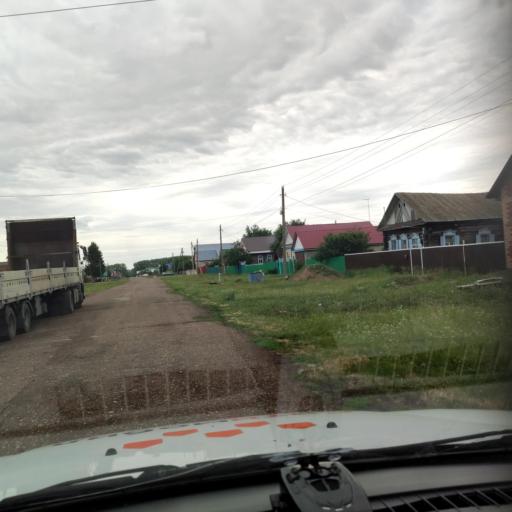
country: RU
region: Bashkortostan
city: Kabakovo
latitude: 54.4551
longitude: 55.9533
